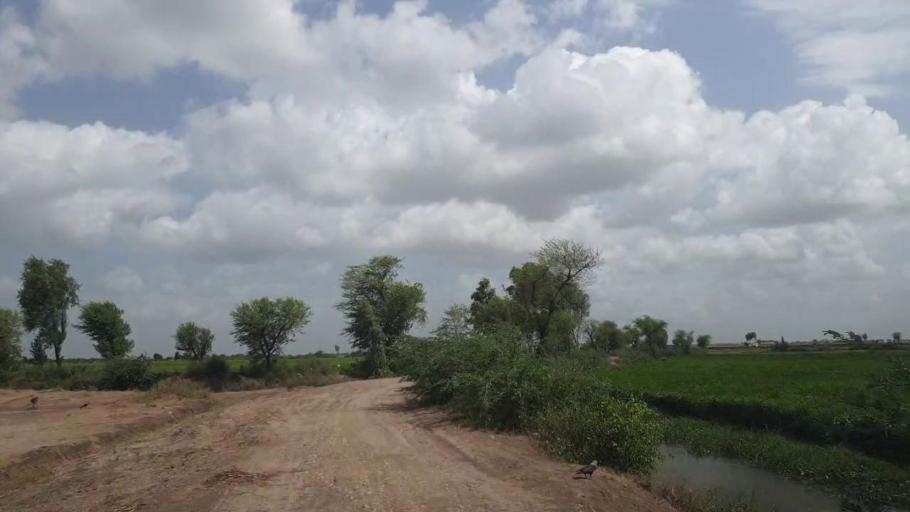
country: PK
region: Sindh
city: Tando Bago
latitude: 24.6534
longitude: 68.9981
